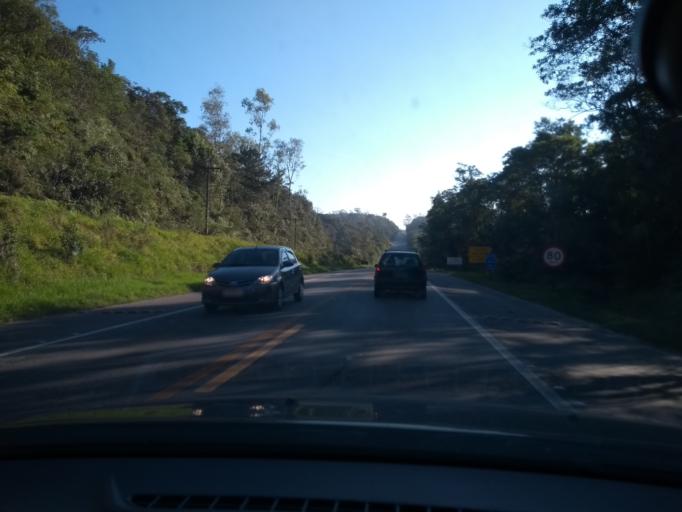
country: BR
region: Sao Paulo
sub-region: Rio Grande Da Serra
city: Rio Grande da Serra
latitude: -23.7761
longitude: -46.4808
